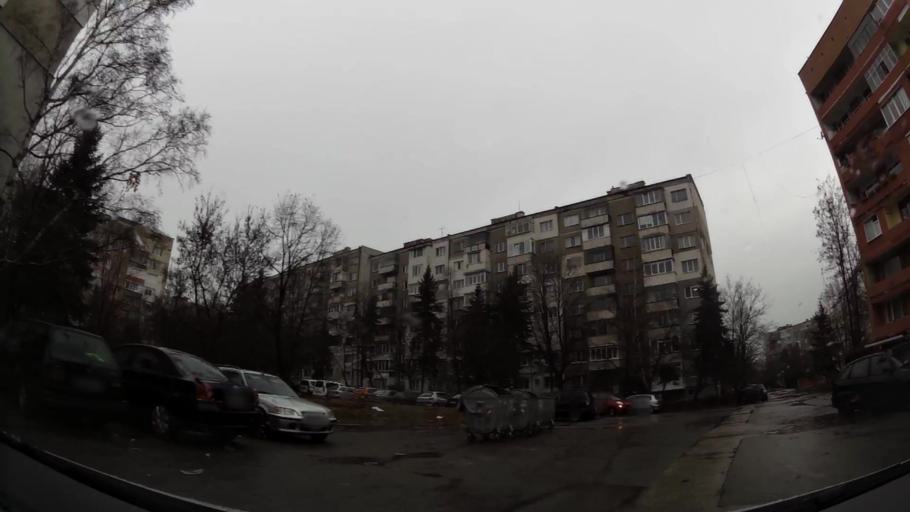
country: BG
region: Sofia-Capital
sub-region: Stolichna Obshtina
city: Sofia
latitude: 42.6524
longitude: 23.3703
